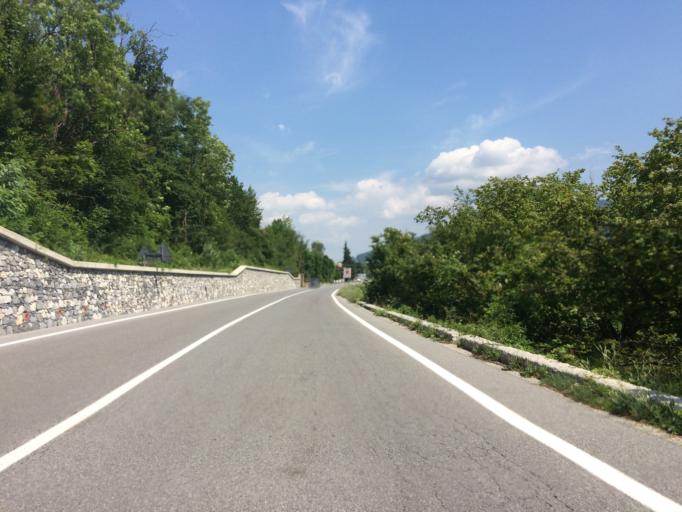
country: IT
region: Piedmont
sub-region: Provincia di Cuneo
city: Garessio
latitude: 44.1969
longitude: 8.0115
